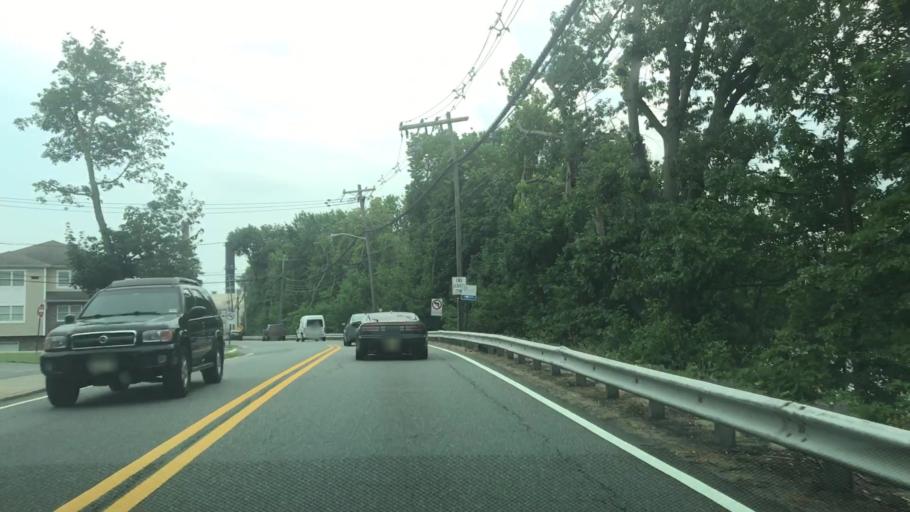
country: US
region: New Jersey
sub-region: Bergen County
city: Elmwood Park
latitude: 40.9087
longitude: -74.1313
